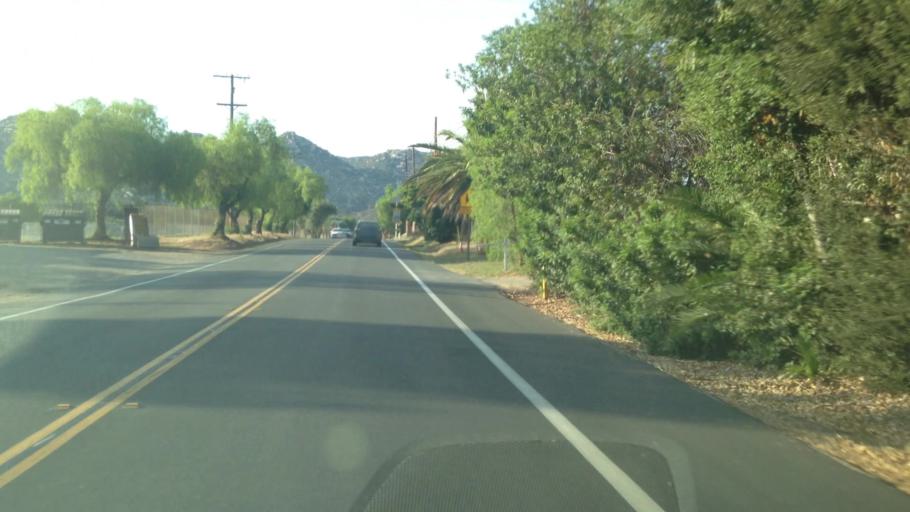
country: US
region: California
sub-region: San Diego County
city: Rainbow
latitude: 33.4119
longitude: -117.1476
